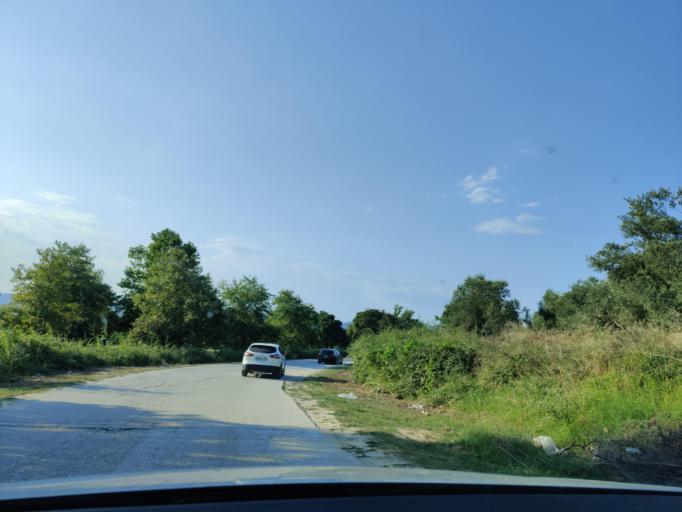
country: GR
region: East Macedonia and Thrace
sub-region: Nomos Kavalas
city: Nea Peramos
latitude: 40.8245
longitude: 24.3074
